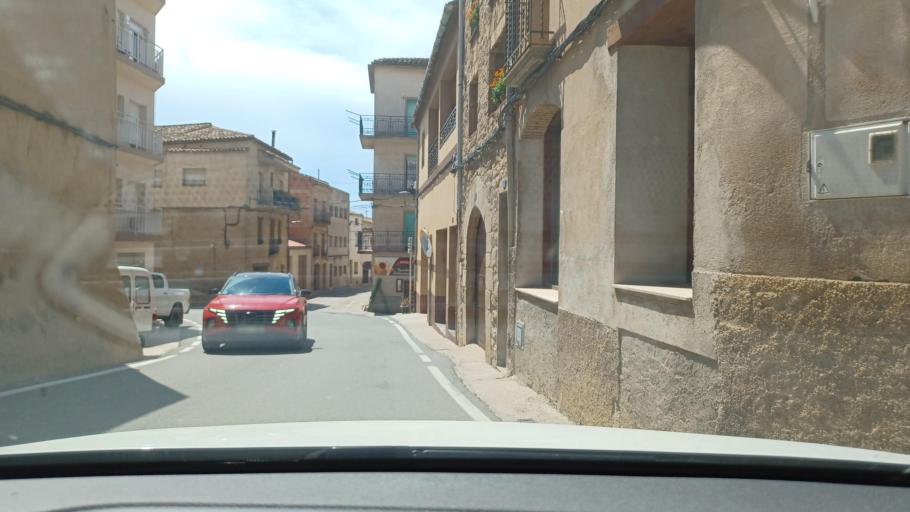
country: ES
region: Catalonia
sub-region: Provincia de Tarragona
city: Horta de Sant Joan
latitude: 40.9555
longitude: 0.3149
